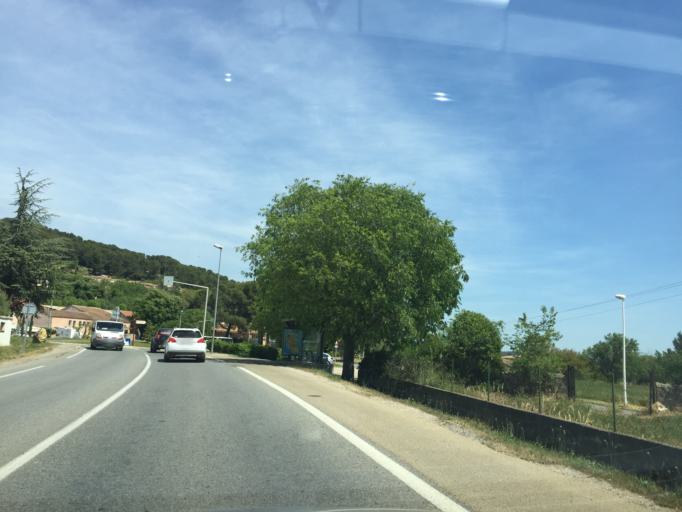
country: FR
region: Provence-Alpes-Cote d'Azur
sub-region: Departement du Var
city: Lorgues
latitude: 43.4916
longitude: 6.3674
